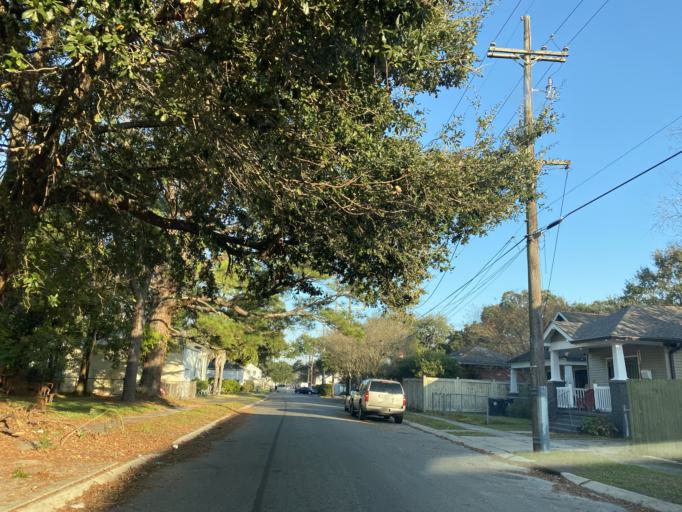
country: US
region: Louisiana
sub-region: Orleans Parish
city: New Orleans
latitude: 29.9947
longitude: -90.0633
